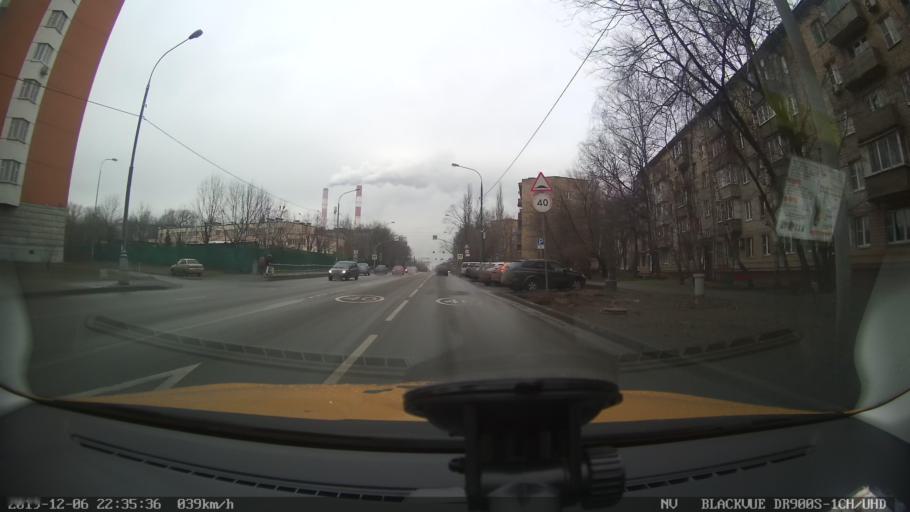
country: RU
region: Moscow
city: Metrogorodok
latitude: 55.8110
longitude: 37.7814
